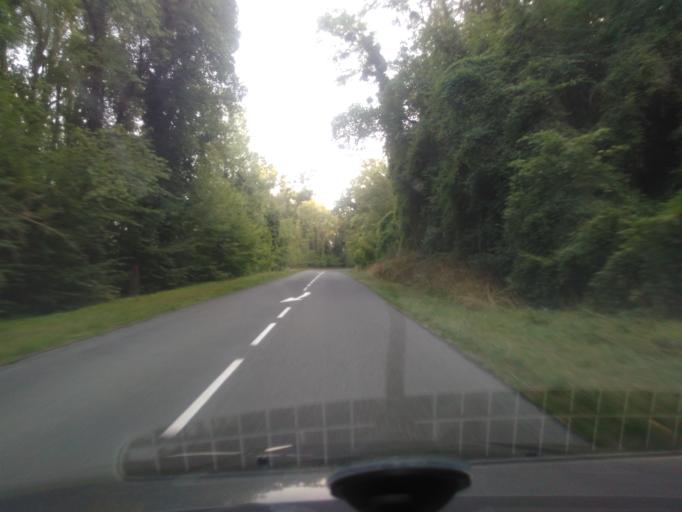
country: FR
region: Picardie
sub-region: Departement de l'Aisne
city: Bruyeres-et-Montberault
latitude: 49.4528
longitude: 3.6684
